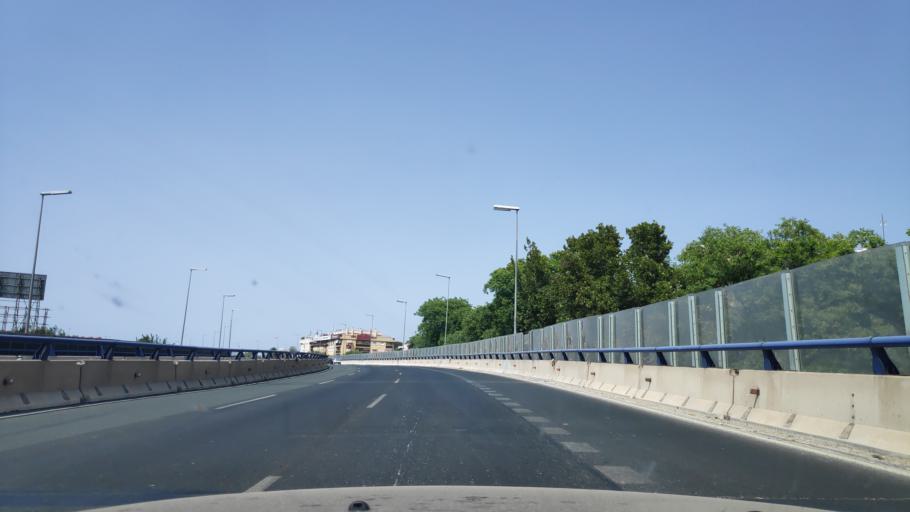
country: ES
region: Murcia
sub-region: Murcia
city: Murcia
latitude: 37.9731
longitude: -1.1370
